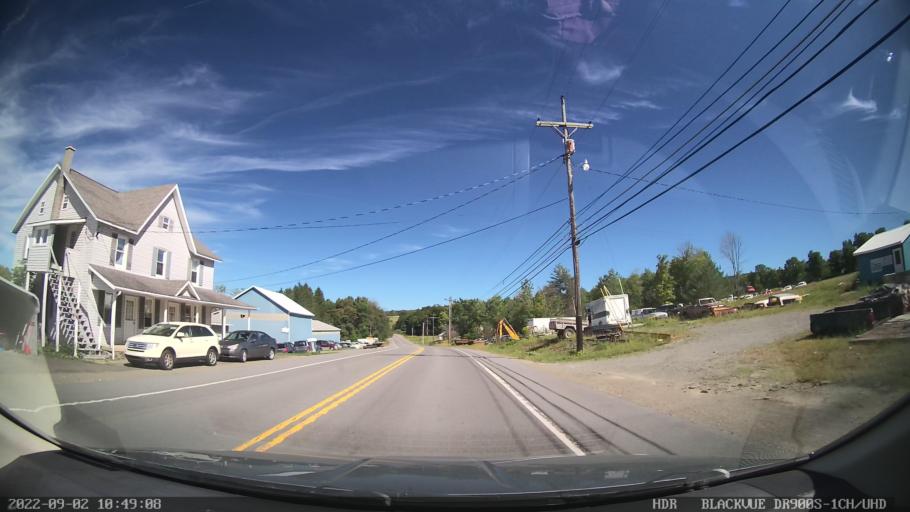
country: US
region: Pennsylvania
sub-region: Tioga County
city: Blossburg
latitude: 41.5962
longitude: -77.1101
